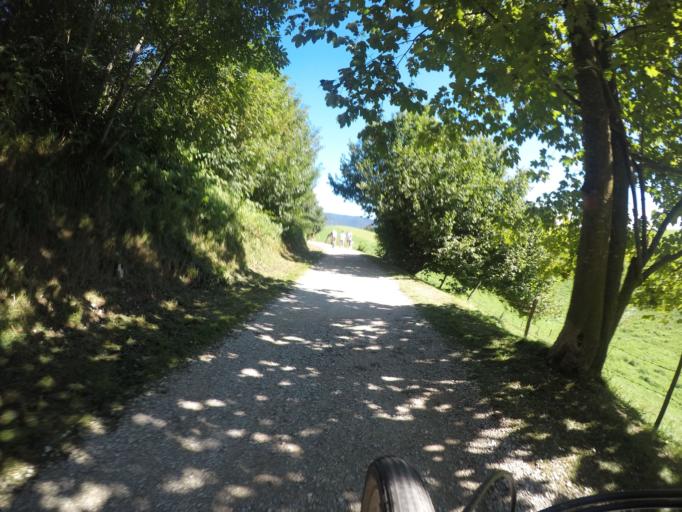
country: IT
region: Veneto
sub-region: Provincia di Vicenza
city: Canove di Roana
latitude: 45.8593
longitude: 11.4765
